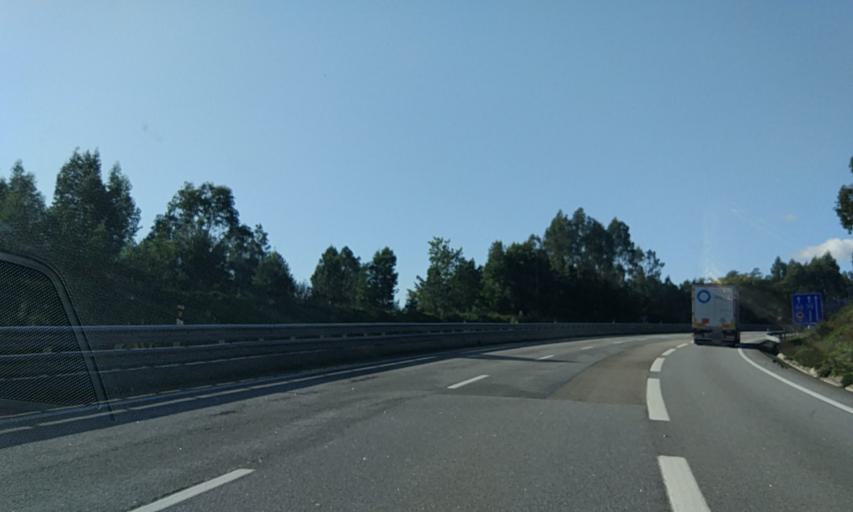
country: PT
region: Aveiro
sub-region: Sever do Vouga
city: Sever do Vouga
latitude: 40.6775
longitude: -8.2835
